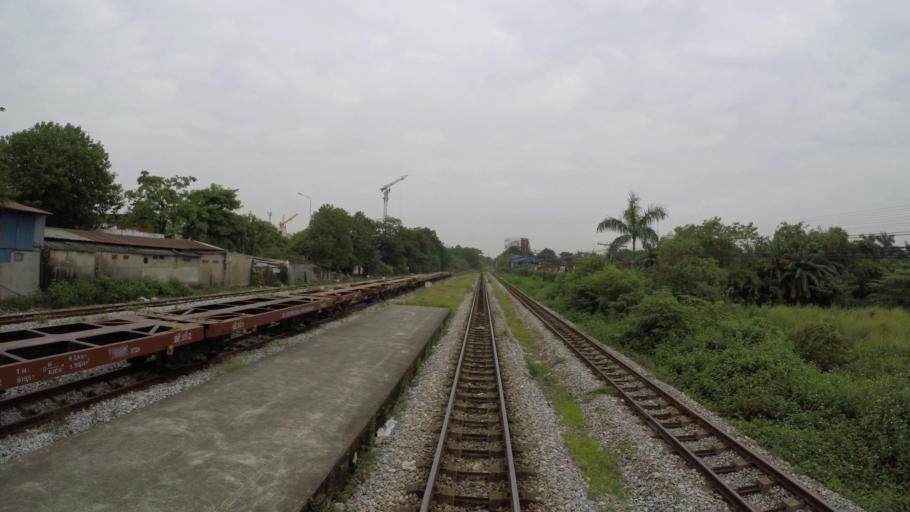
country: VN
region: Hai Phong
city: An Duong
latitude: 20.8805
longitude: 106.6209
